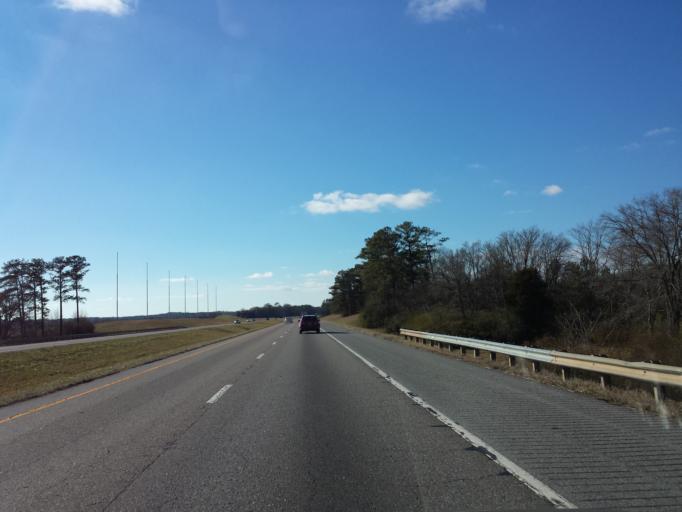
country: US
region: Alabama
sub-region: Talladega County
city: Lincoln
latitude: 33.5852
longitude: -86.0589
